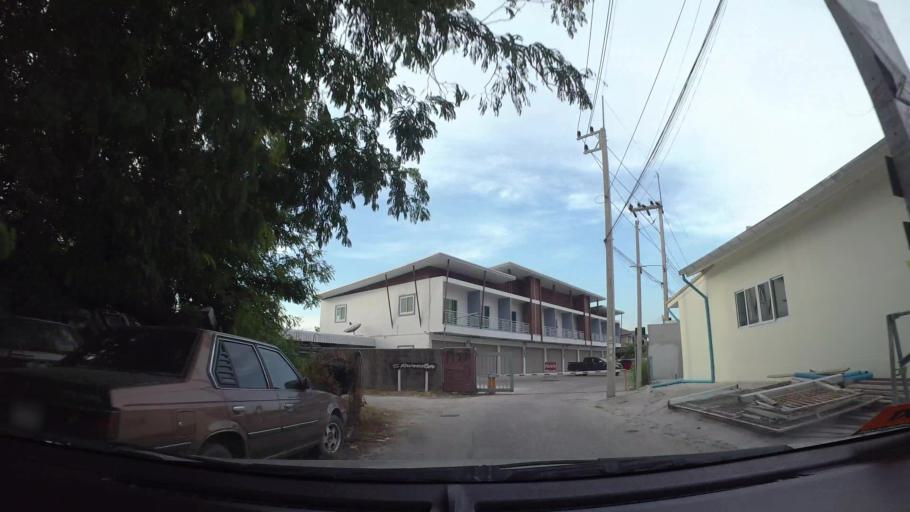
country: TH
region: Chon Buri
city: Chon Buri
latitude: 13.3362
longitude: 100.9819
